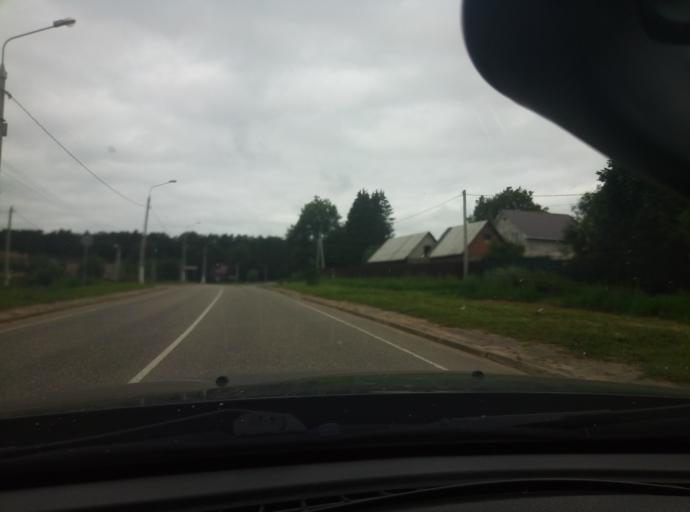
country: RU
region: Kaluga
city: Zhukovo
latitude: 54.9644
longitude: 36.7906
